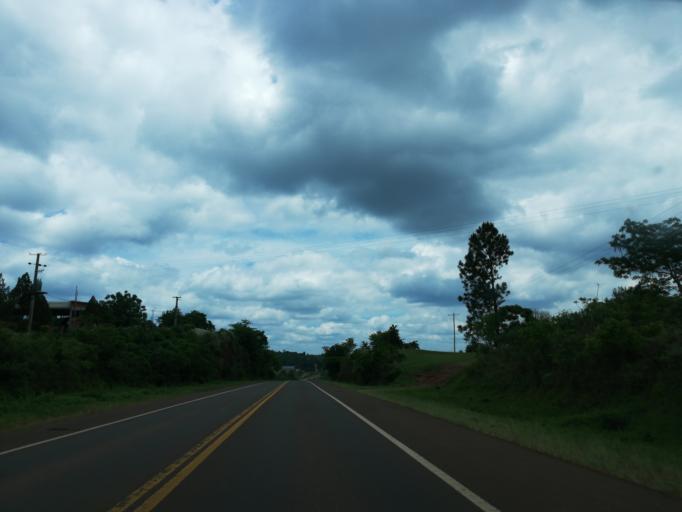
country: AR
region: Misiones
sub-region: Departamento de Leandro N. Alem
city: Leandro N. Alem
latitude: -27.6347
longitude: -55.3443
